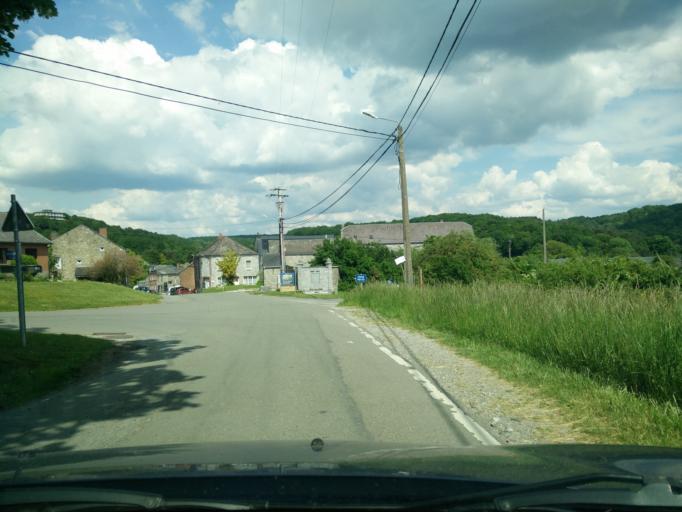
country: BE
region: Wallonia
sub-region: Province de Namur
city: Couvin
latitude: 50.0902
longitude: 4.5882
